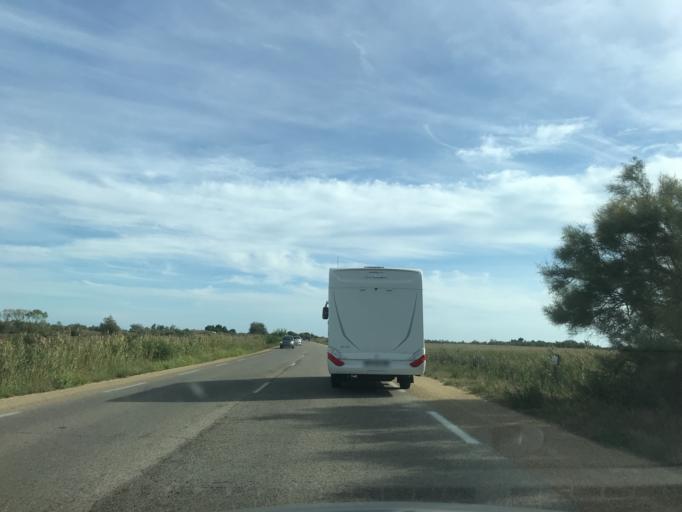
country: FR
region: Provence-Alpes-Cote d'Azur
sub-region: Departement des Bouches-du-Rhone
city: Saintes-Maries-de-la-Mer
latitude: 43.5102
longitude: 4.3990
